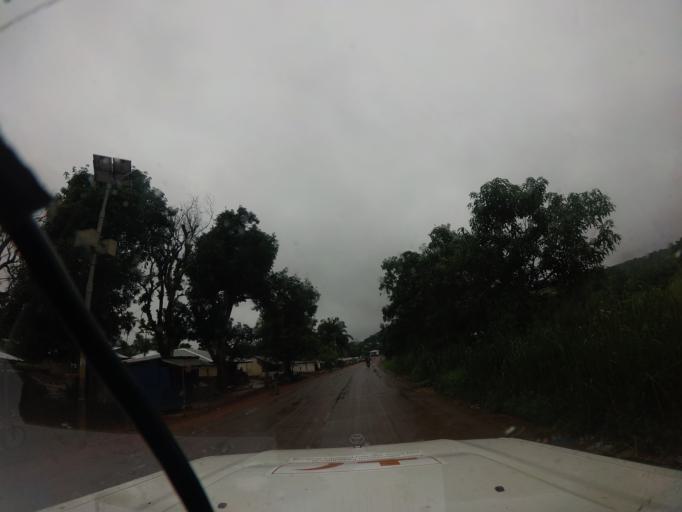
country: SL
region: Northern Province
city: Kabala
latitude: 9.5758
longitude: -11.5569
